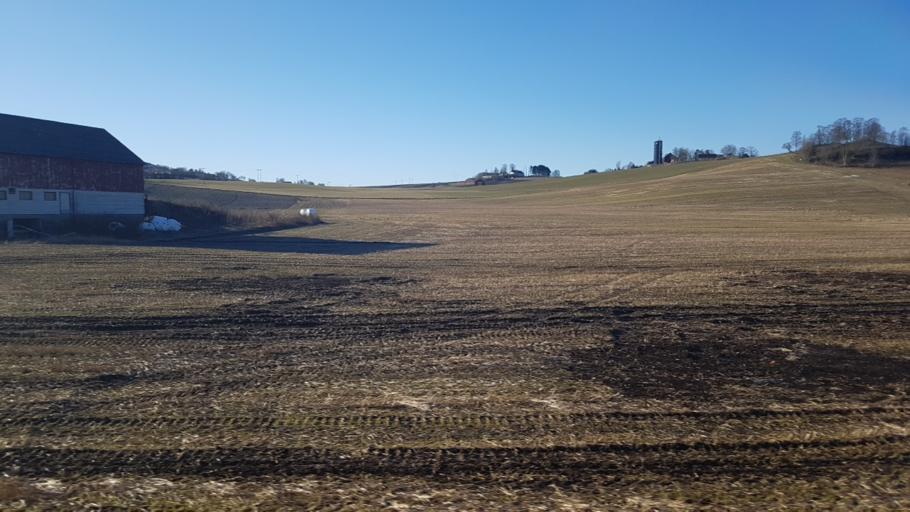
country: NO
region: Nord-Trondelag
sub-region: Levanger
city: Levanger
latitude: 63.7276
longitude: 11.2600
